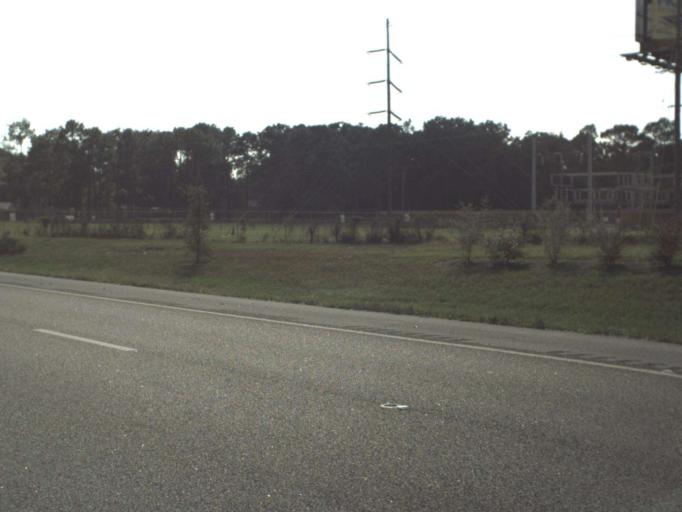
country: US
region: Florida
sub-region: Escambia County
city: Brent
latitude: 30.4676
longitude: -87.2273
